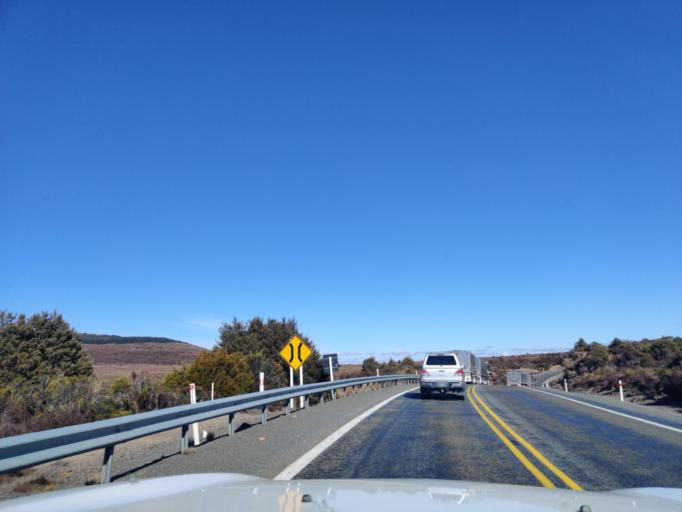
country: NZ
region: Manawatu-Wanganui
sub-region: Ruapehu District
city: Waiouru
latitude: -39.2798
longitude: 175.7444
